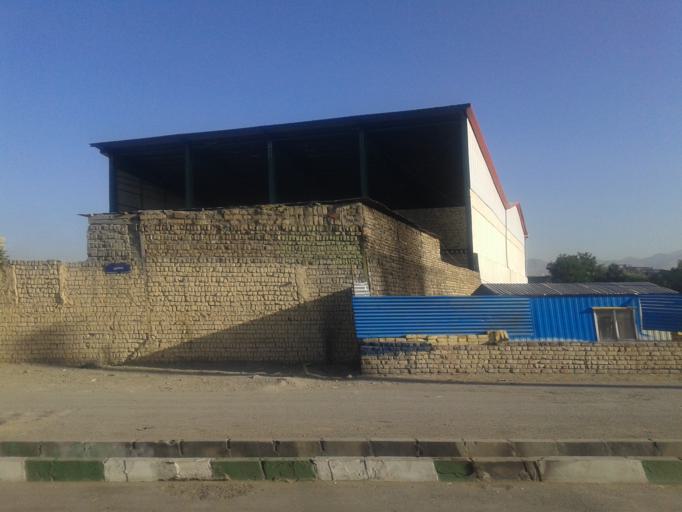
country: IR
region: Tehran
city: Rey
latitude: 35.6180
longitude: 51.3600
